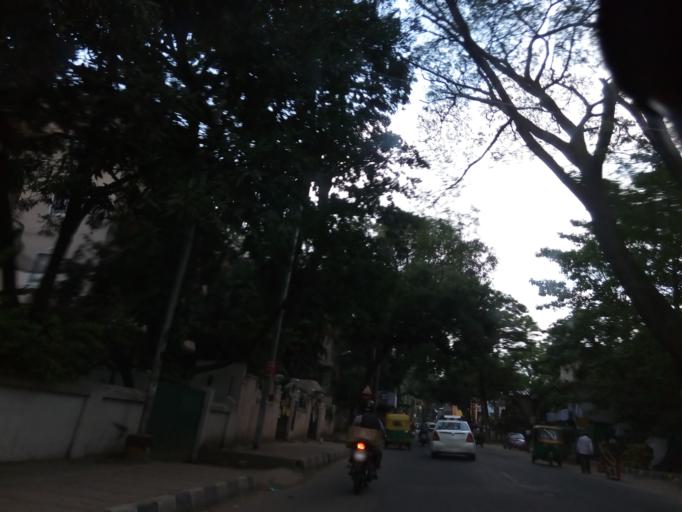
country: IN
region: Karnataka
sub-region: Bangalore Urban
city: Bangalore
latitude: 13.0011
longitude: 77.5994
